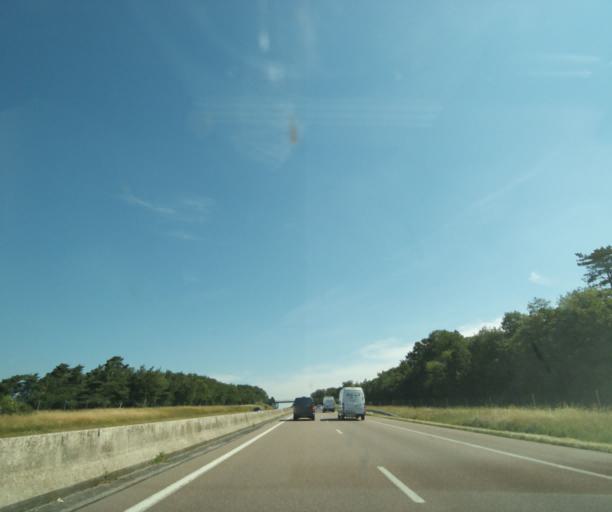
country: FR
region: Lorraine
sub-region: Departement de Meurthe-et-Moselle
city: Colombey-les-Belles
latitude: 48.4385
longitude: 5.8634
